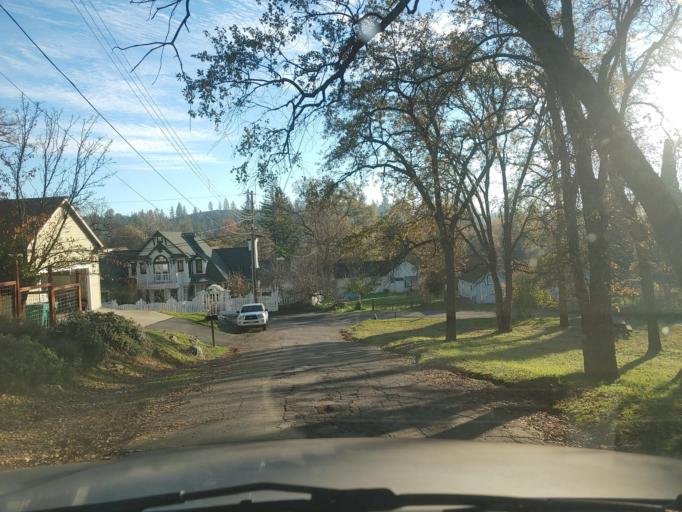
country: US
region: California
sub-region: Tuolumne County
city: Columbia
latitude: 38.0371
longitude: -120.3989
